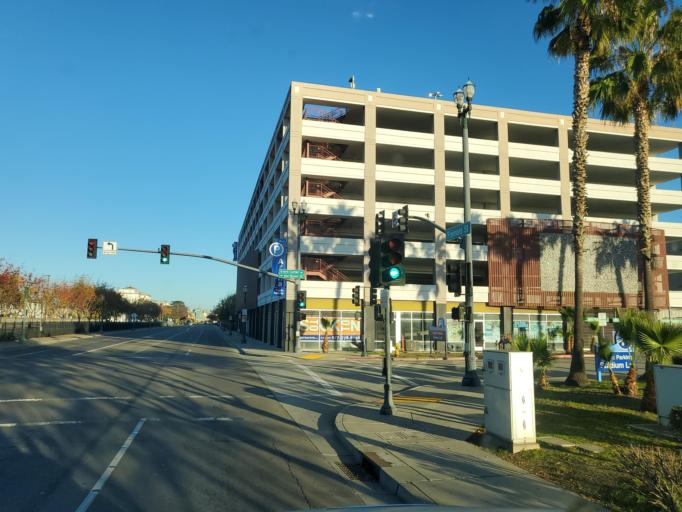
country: US
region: California
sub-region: San Joaquin County
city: Stockton
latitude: 37.9565
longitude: -121.2979
